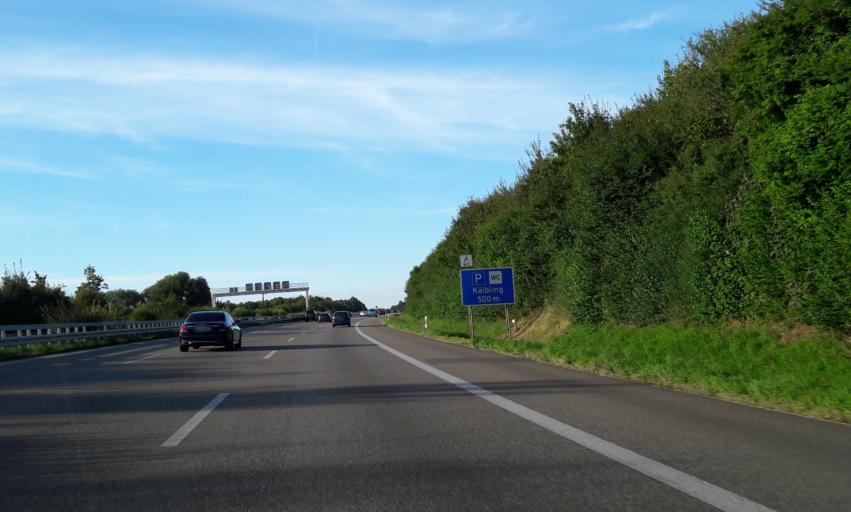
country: DE
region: Baden-Wuerttemberg
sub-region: Regierungsbezirk Stuttgart
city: Mundelsheim
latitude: 48.9843
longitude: 9.2303
